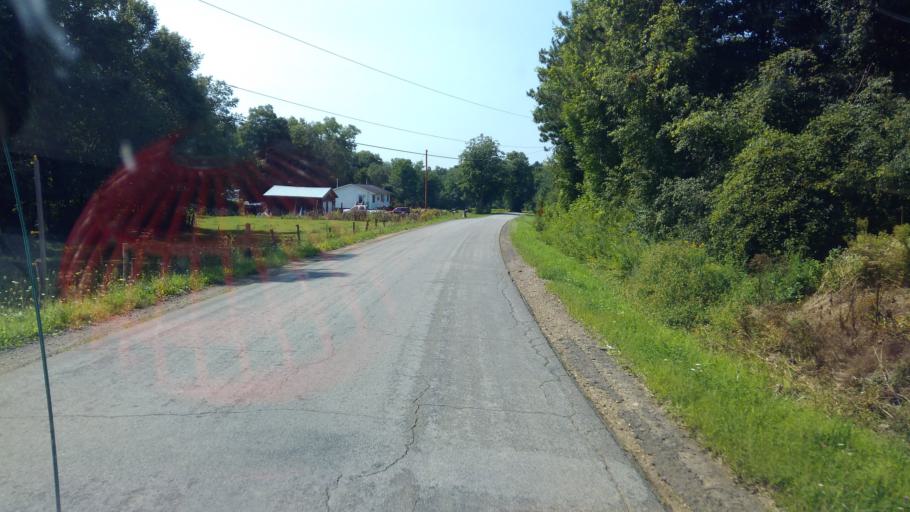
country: US
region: New York
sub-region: Allegany County
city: Belmont
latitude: 42.2545
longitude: -78.0045
